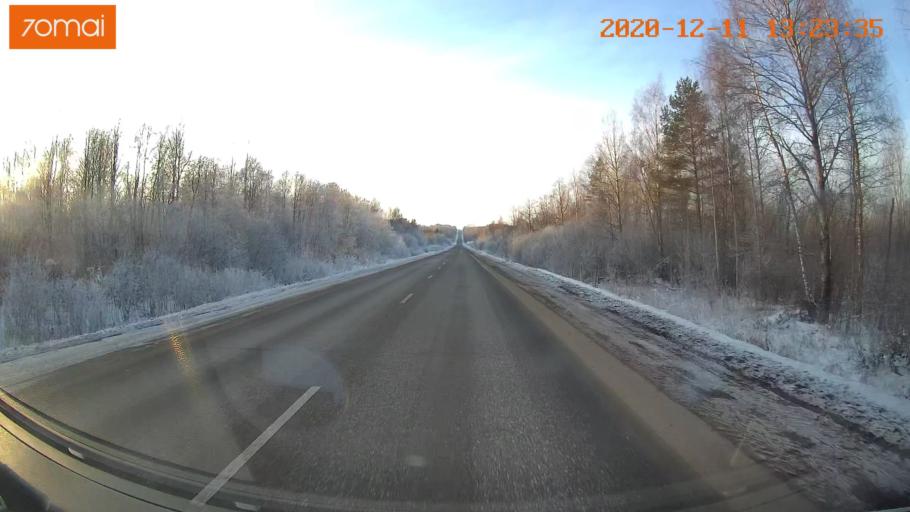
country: RU
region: Kostroma
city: Susanino
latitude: 58.0342
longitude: 41.4713
